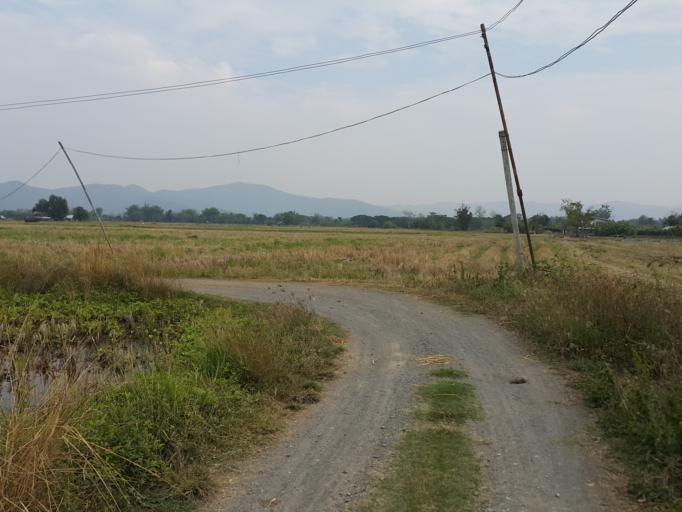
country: TH
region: Chiang Mai
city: San Kamphaeng
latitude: 18.8244
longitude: 99.1479
